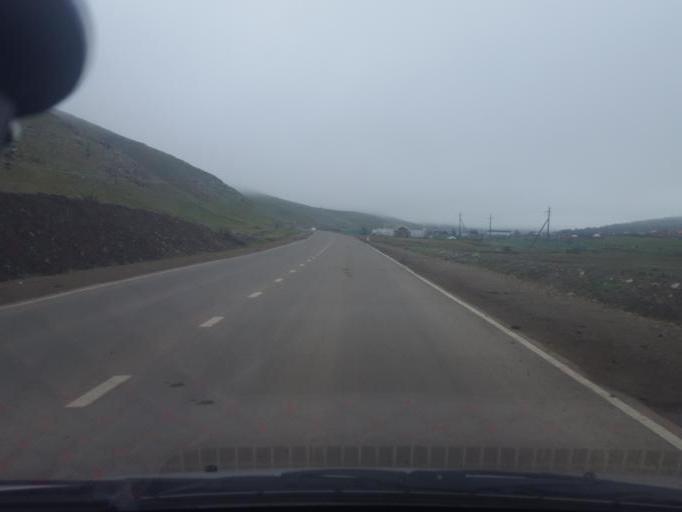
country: MN
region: Ulaanbaatar
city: Ulaanbaatar
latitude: 48.0924
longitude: 106.7772
